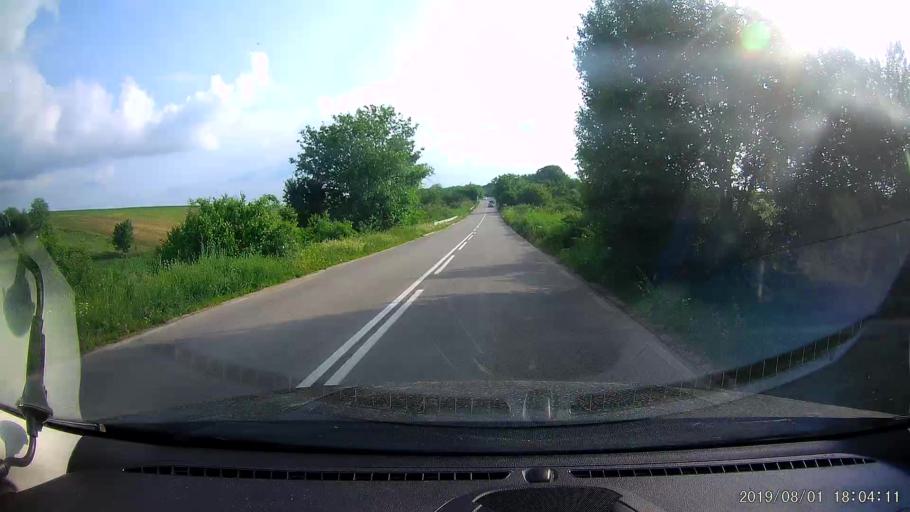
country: BG
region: Silistra
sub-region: Obshtina Alfatar
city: Alfatar
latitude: 43.9124
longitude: 27.2855
